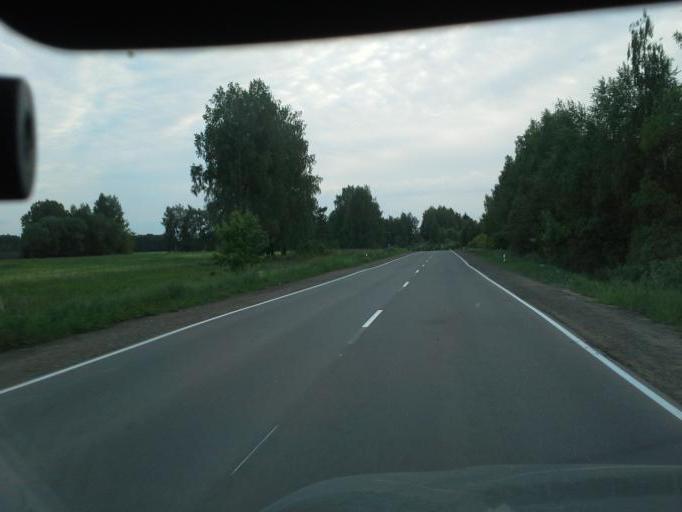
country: RU
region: Ivanovo
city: Petrovskiy
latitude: 56.6215
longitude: 40.2700
